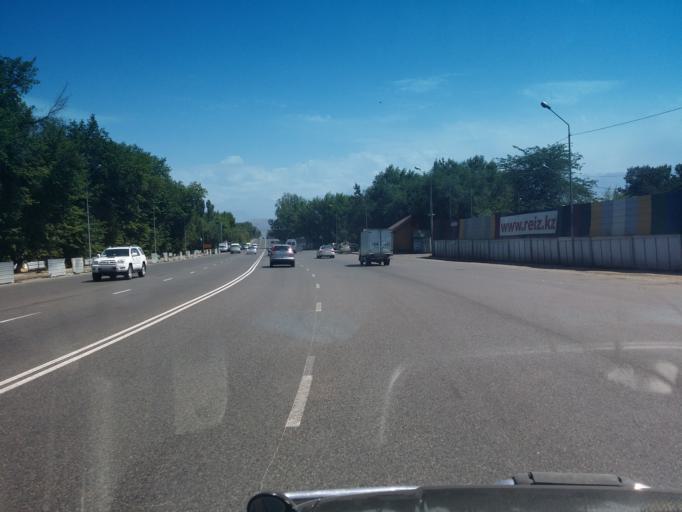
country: KZ
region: Almaty Oblysy
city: Pervomayskiy
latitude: 43.3447
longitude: 76.9717
